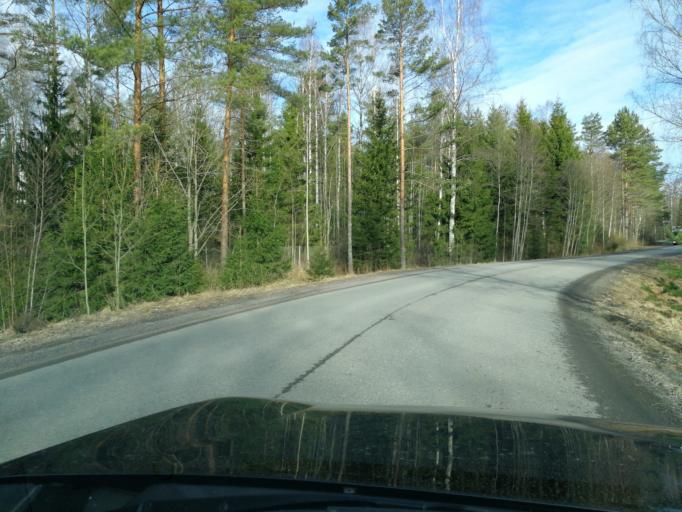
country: FI
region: Uusimaa
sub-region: Helsinki
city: Kirkkonummi
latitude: 60.0915
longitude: 24.3685
